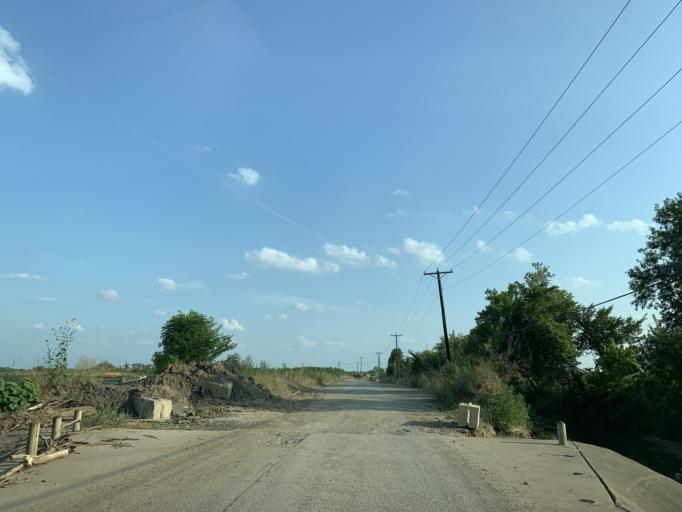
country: US
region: Texas
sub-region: Tarrant County
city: Hurst
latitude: 32.7971
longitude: -97.1693
